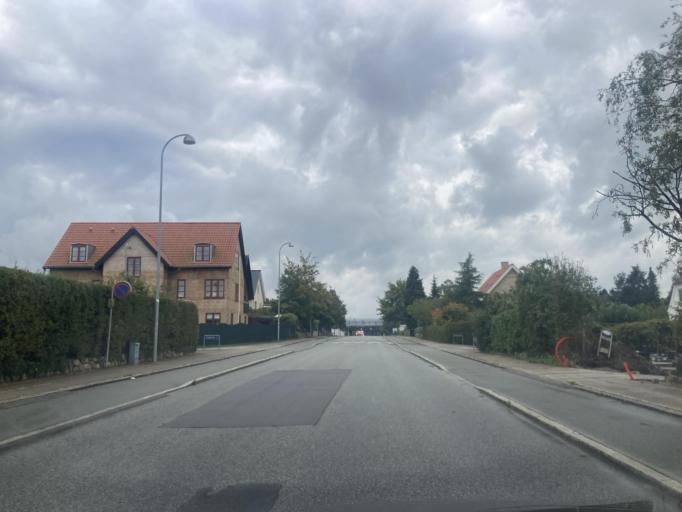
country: DK
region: Capital Region
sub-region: Gladsaxe Municipality
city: Buddinge
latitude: 55.7538
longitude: 12.4832
